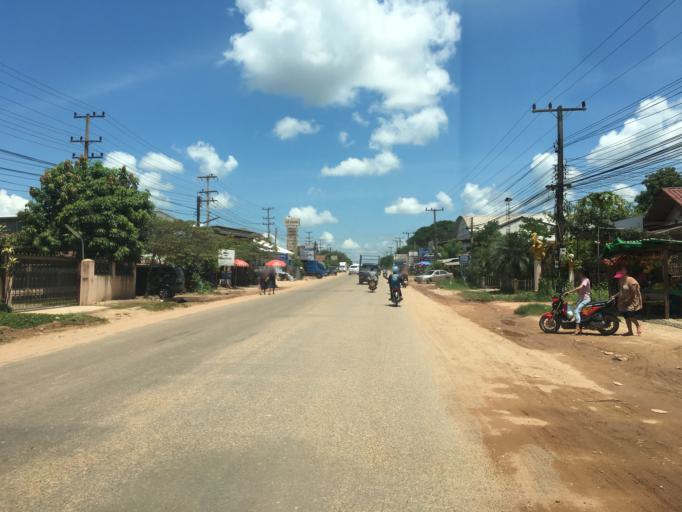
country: LA
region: Vientiane
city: Vientiane
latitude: 18.0391
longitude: 102.5470
